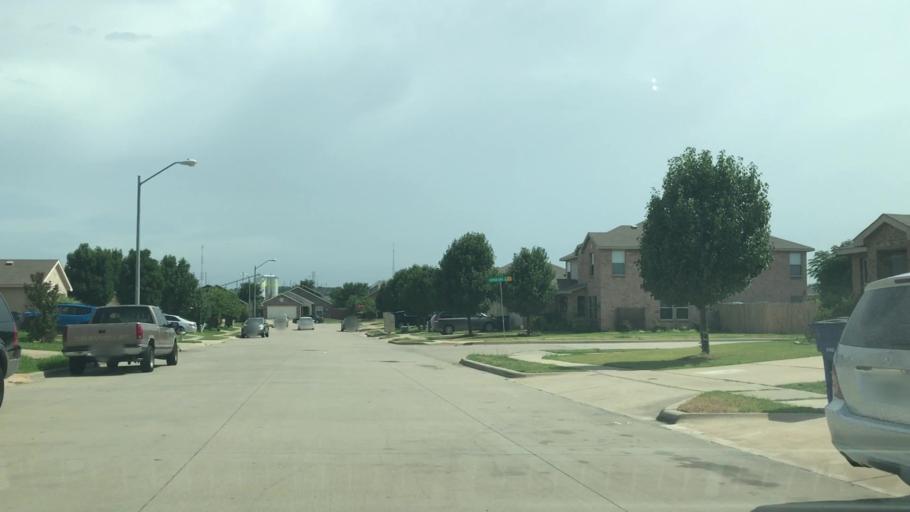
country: US
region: Texas
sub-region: Dallas County
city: Cockrell Hill
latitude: 32.7852
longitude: -96.8716
